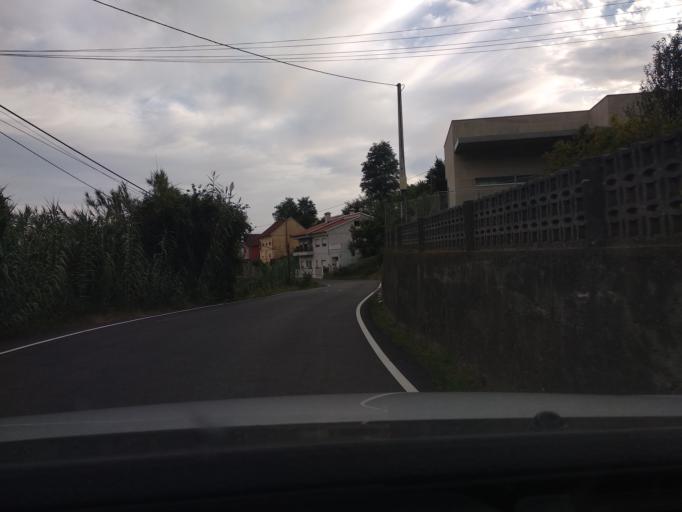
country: ES
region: Galicia
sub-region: Provincia de Pontevedra
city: Moana
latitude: 42.2970
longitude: -8.7390
